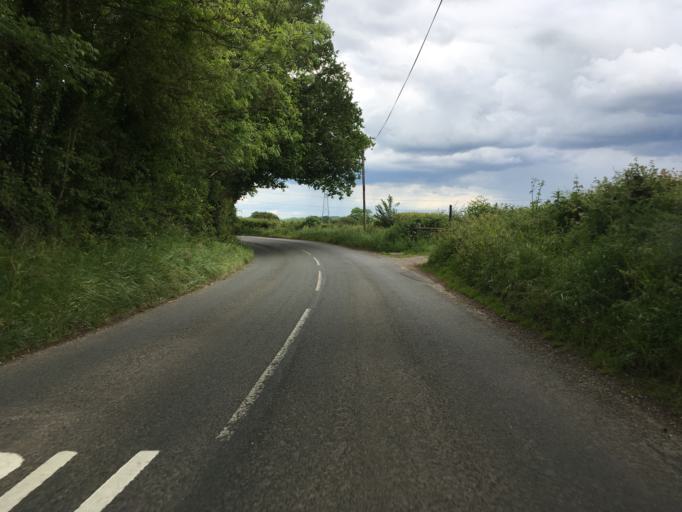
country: GB
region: England
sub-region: Wiltshire
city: Hankerton
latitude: 51.6427
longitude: -2.0034
